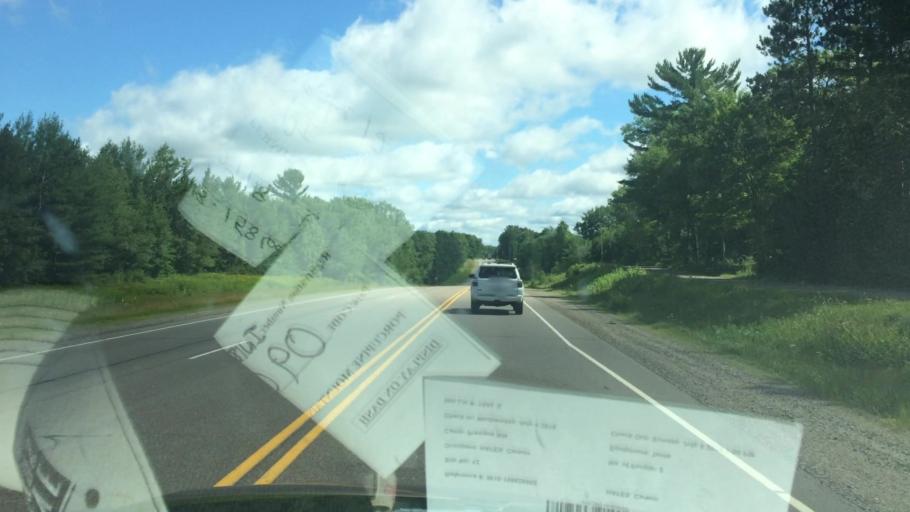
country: US
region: Wisconsin
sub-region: Oneida County
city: Rhinelander
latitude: 45.6003
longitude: -89.5604
